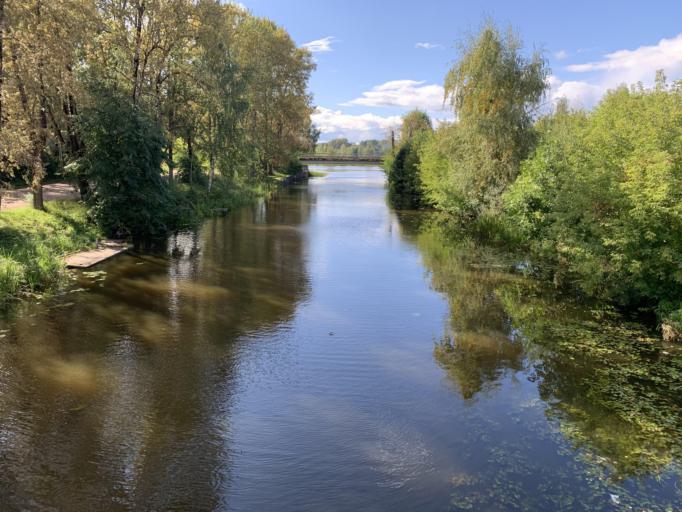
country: RU
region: Tverskaya
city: Vyshniy Volochek
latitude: 57.5786
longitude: 34.5598
